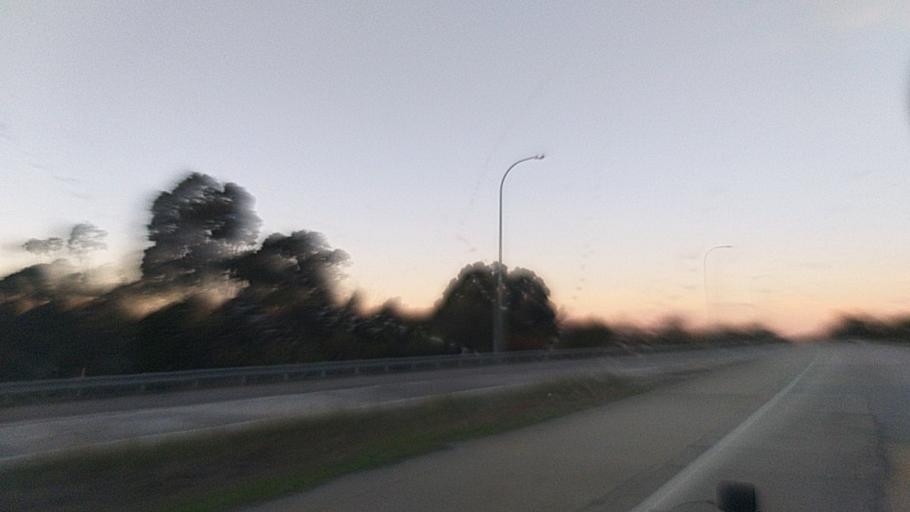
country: AU
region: New South Wales
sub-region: Wingecarribee
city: Bundanoon
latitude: -34.7077
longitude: 150.0123
